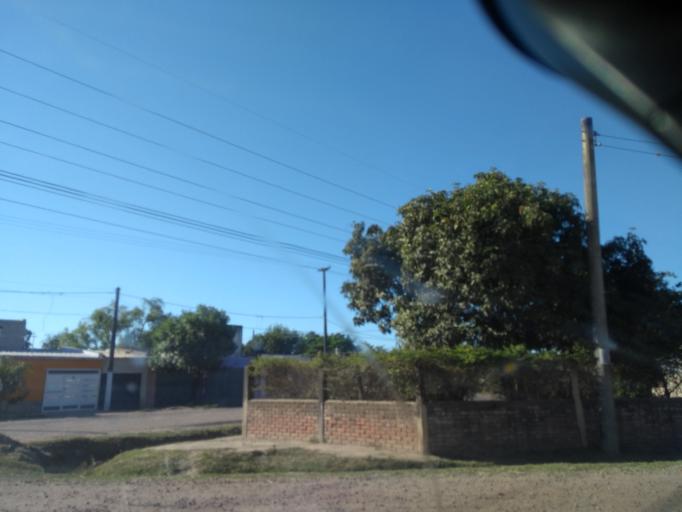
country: AR
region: Chaco
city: Resistencia
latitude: -27.4750
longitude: -58.9705
